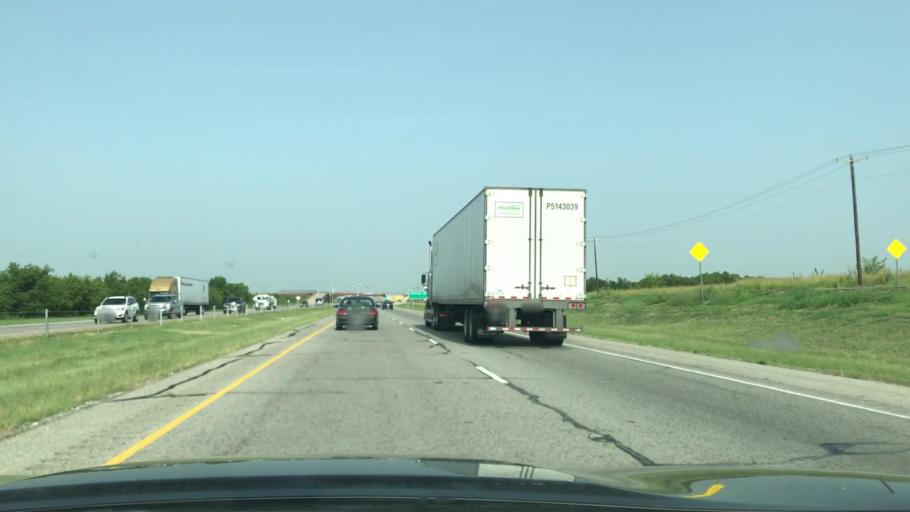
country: US
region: Texas
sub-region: Kaufman County
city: Talty
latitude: 32.7403
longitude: -96.4036
